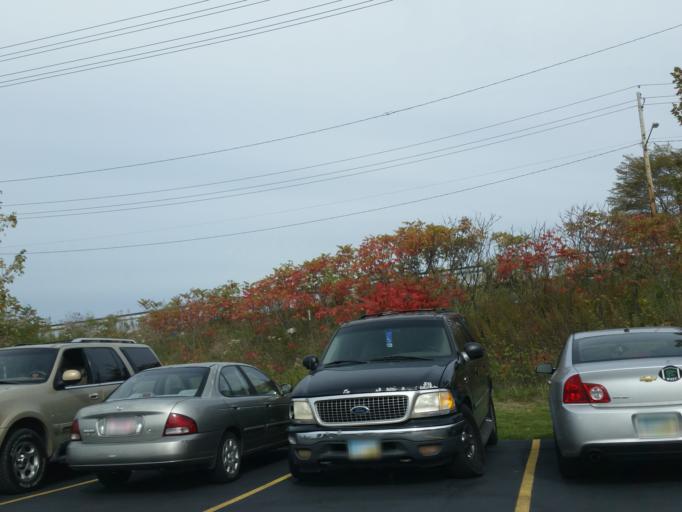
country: US
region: Ohio
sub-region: Cuyahoga County
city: Newburgh Heights
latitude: 41.4745
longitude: -81.6288
